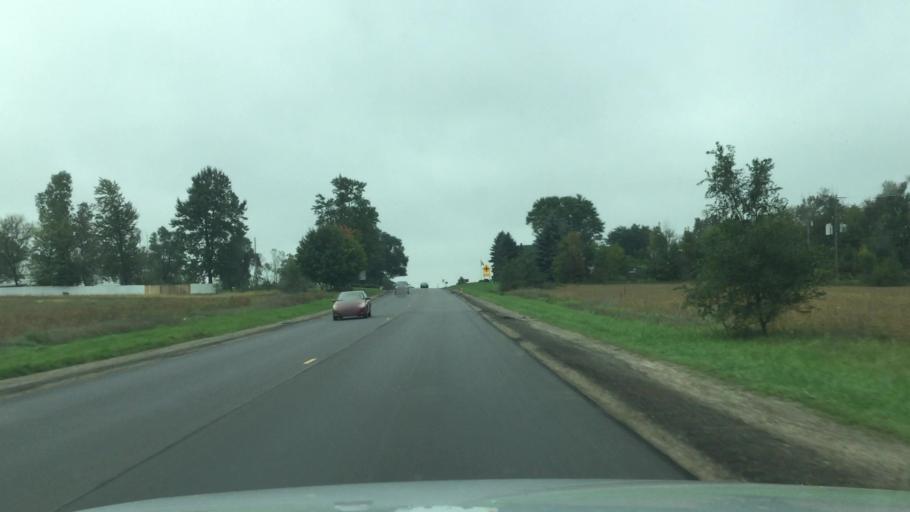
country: US
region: Michigan
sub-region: Shiawassee County
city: Perry
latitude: 42.8667
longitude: -84.2213
